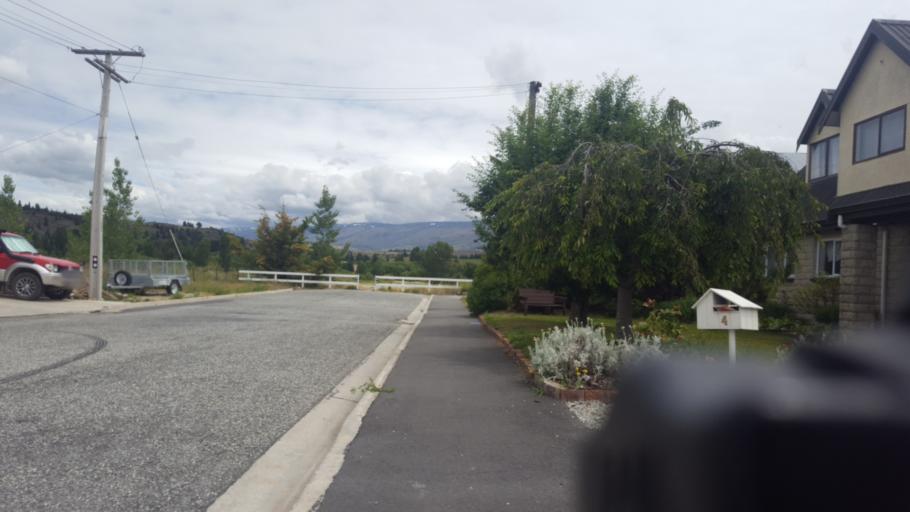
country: NZ
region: Otago
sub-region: Queenstown-Lakes District
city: Wanaka
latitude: -45.2504
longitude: 169.3793
